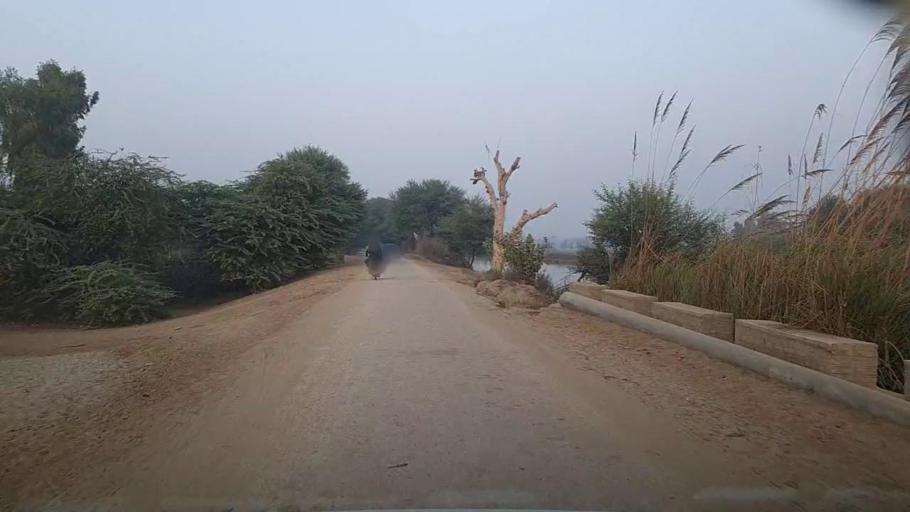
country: PK
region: Sindh
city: Bozdar
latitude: 27.0504
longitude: 68.5964
